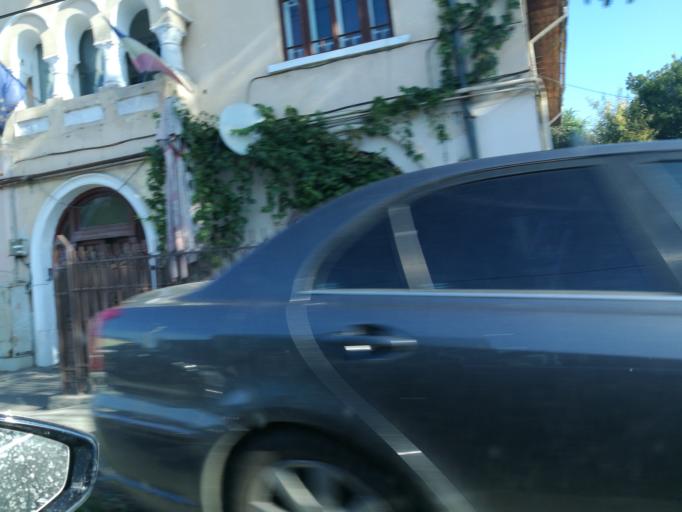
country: RO
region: Iasi
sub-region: Municipiul Iasi
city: Iasi
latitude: 47.1721
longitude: 27.5672
